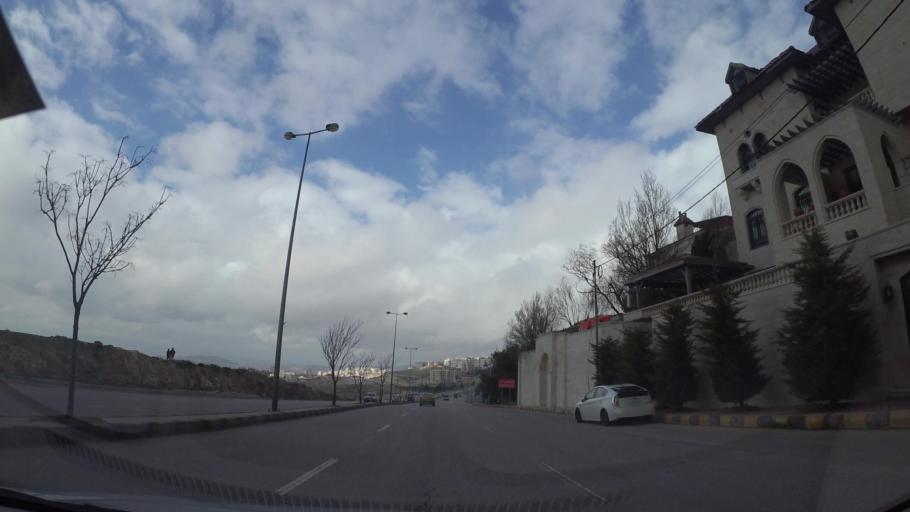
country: JO
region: Amman
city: Al Jubayhah
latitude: 32.0429
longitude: 35.8691
